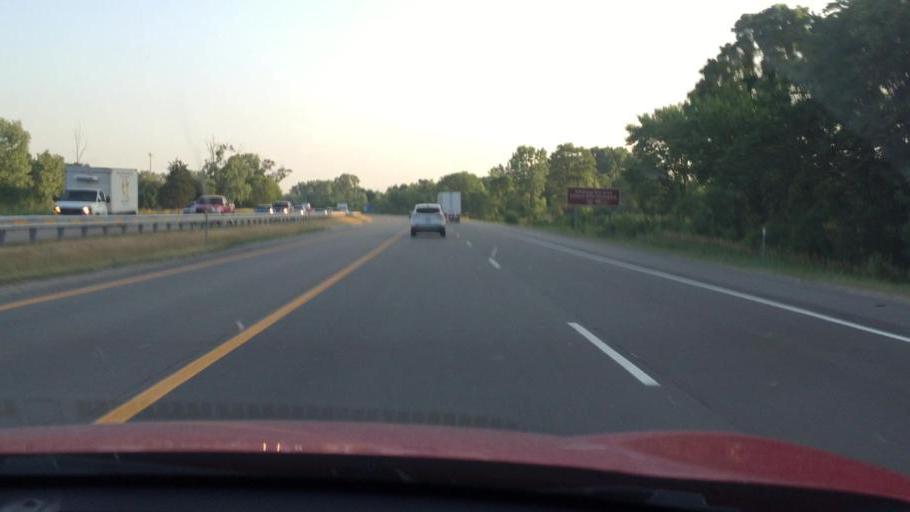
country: US
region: Michigan
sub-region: Livingston County
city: Whitmore Lake
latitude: 42.3657
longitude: -83.7497
